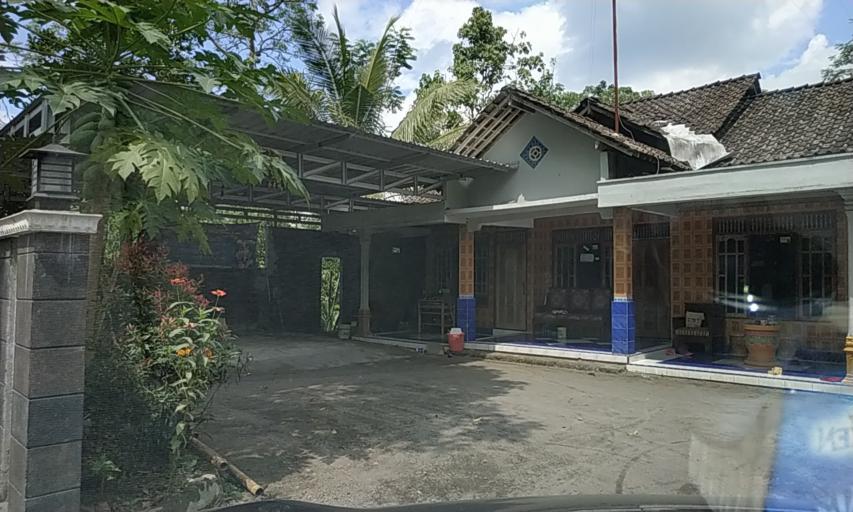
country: ID
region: Central Java
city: Jogonalan
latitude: -7.6344
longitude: 110.4861
